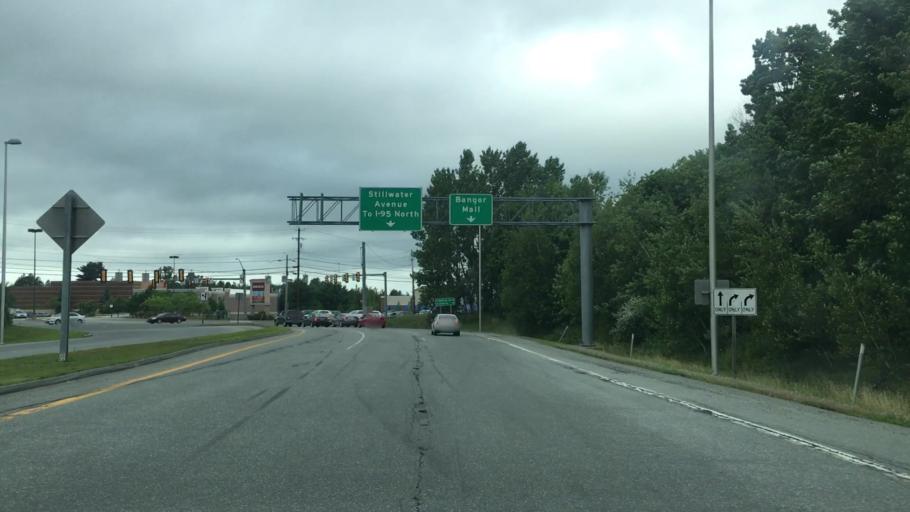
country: US
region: Maine
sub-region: Penobscot County
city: Brewer
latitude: 44.8276
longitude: -68.7544
